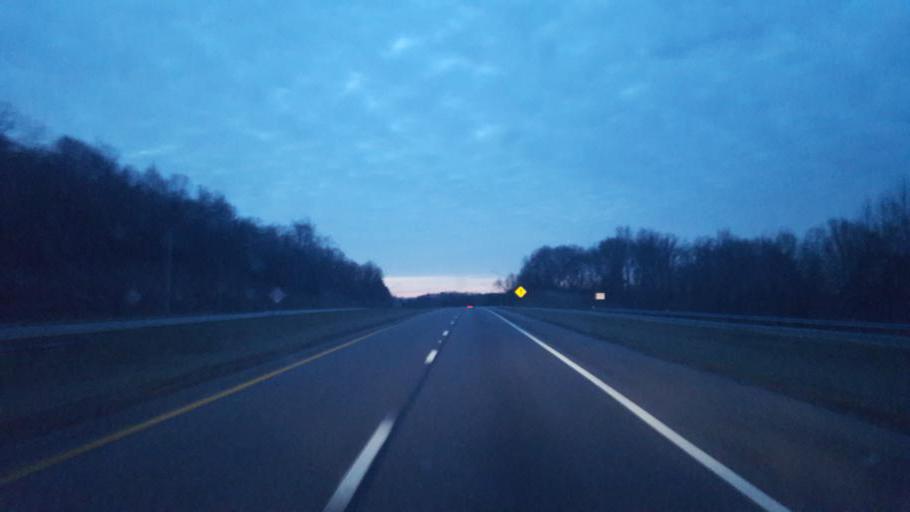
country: US
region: Ohio
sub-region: Jackson County
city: Jackson
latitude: 39.0705
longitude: -82.6279
